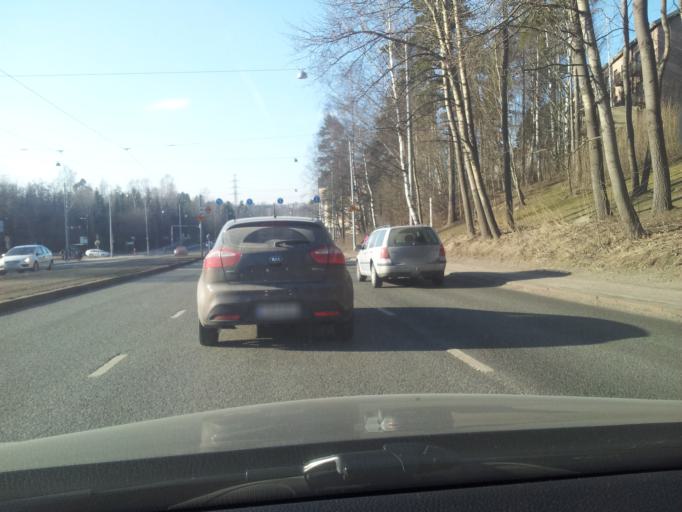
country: FI
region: Uusimaa
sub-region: Helsinki
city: Helsinki
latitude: 60.1925
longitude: 24.8971
